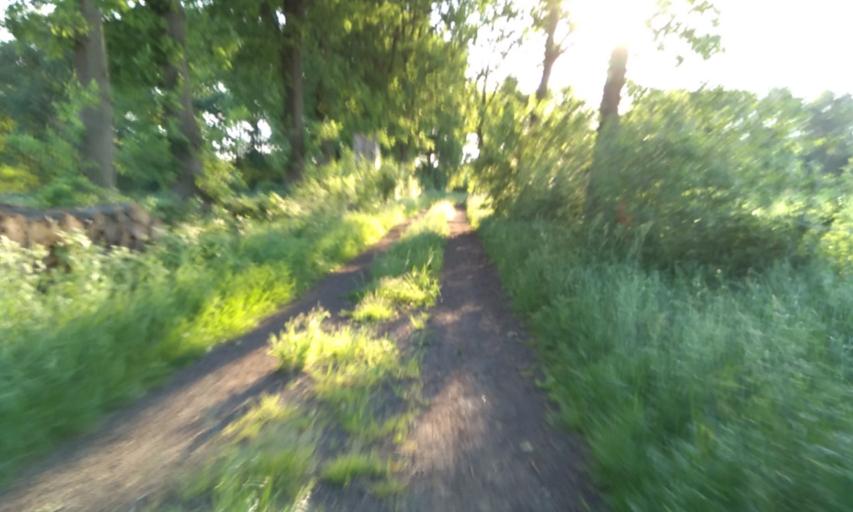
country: DE
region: Lower Saxony
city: Agathenburg
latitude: 53.5381
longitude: 9.5220
